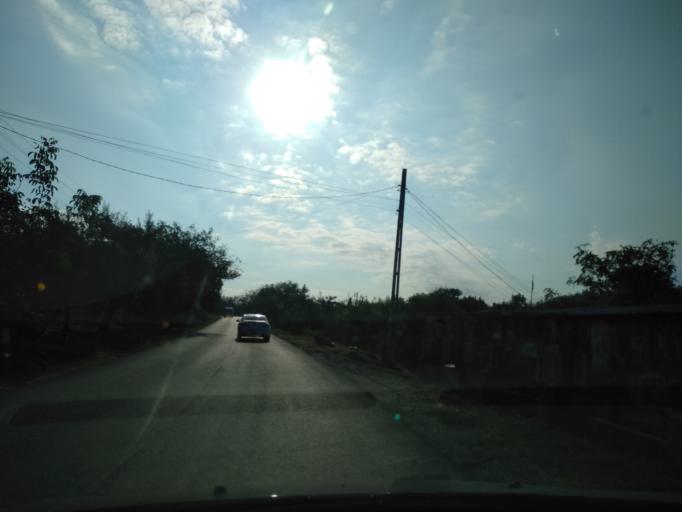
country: RO
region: Giurgiu
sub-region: Comuna Hotarele
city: Hotarele
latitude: 44.1701
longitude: 26.3688
